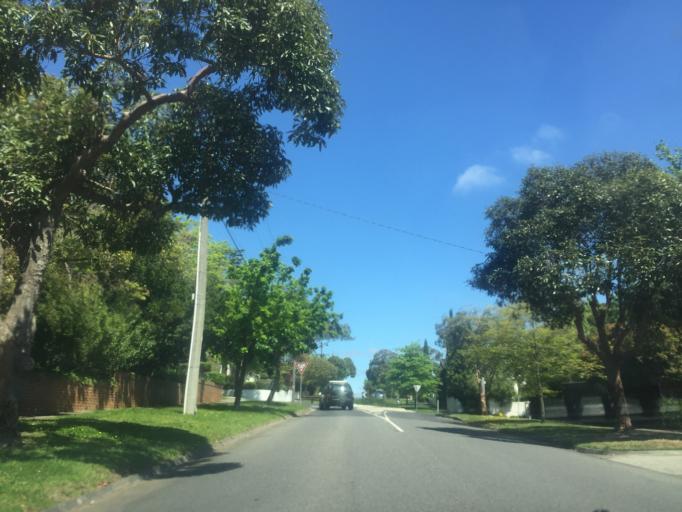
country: AU
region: Victoria
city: Mont Albert
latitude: -37.8096
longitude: 145.0959
